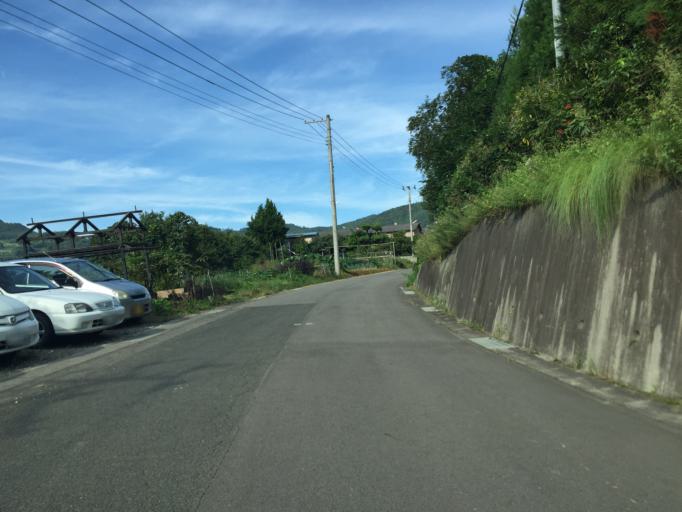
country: JP
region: Fukushima
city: Fukushima-shi
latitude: 37.8340
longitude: 140.4624
